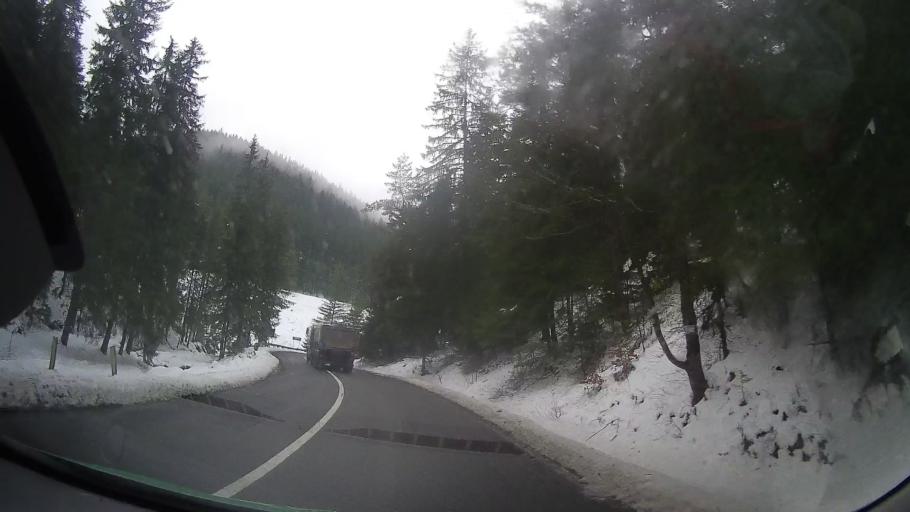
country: RO
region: Neamt
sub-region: Comuna Bicaz Chei
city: Bicaz Chei
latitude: 46.7784
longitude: 25.7659
